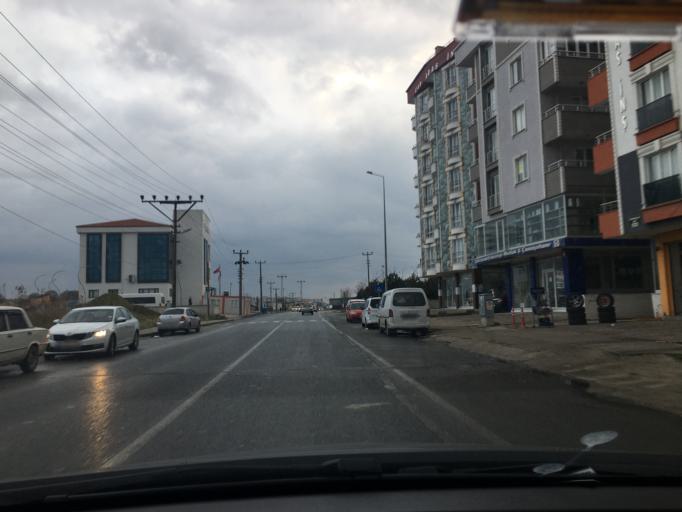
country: TR
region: Tekirdag
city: Cerkezkoey
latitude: 41.2796
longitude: 27.9894
